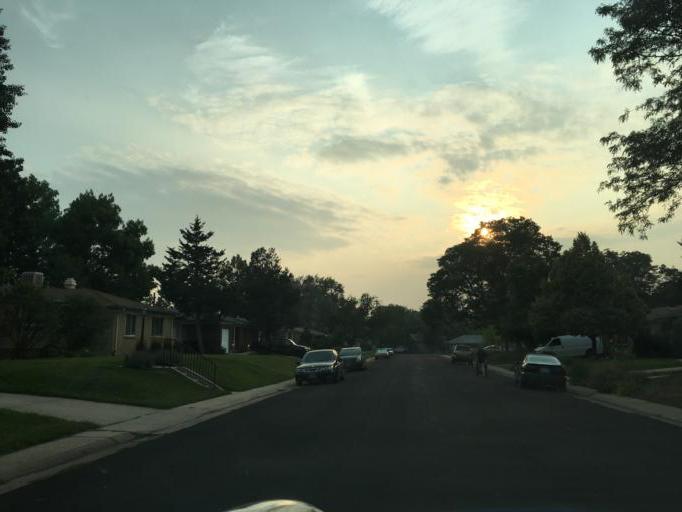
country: US
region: Colorado
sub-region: Arapahoe County
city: Glendale
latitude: 39.6844
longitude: -104.9242
